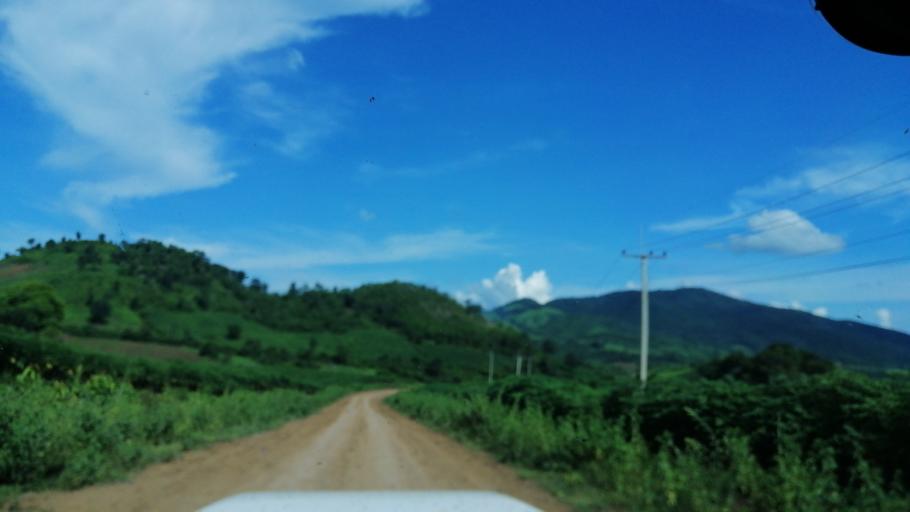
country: TH
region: Uttaradit
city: Ban Khok
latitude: 17.9052
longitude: 101.2068
